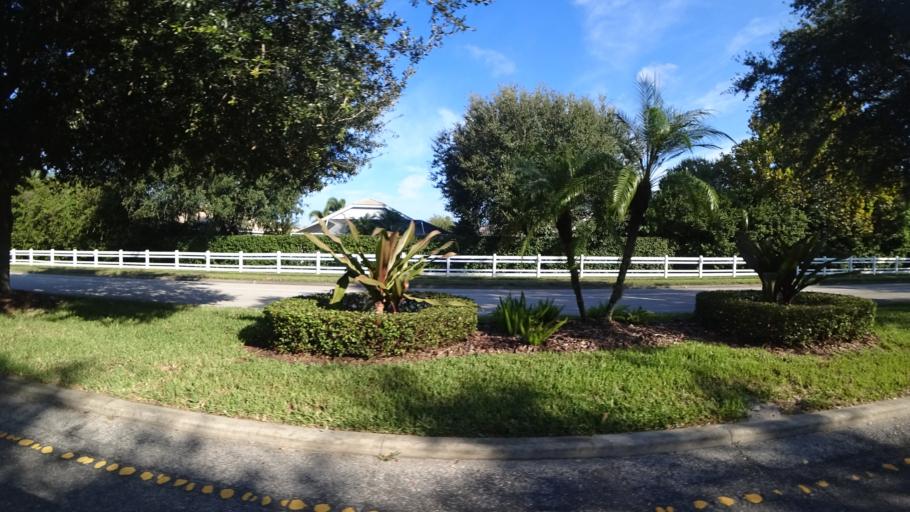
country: US
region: Florida
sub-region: Sarasota County
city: Desoto Lakes
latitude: 27.4176
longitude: -82.4819
